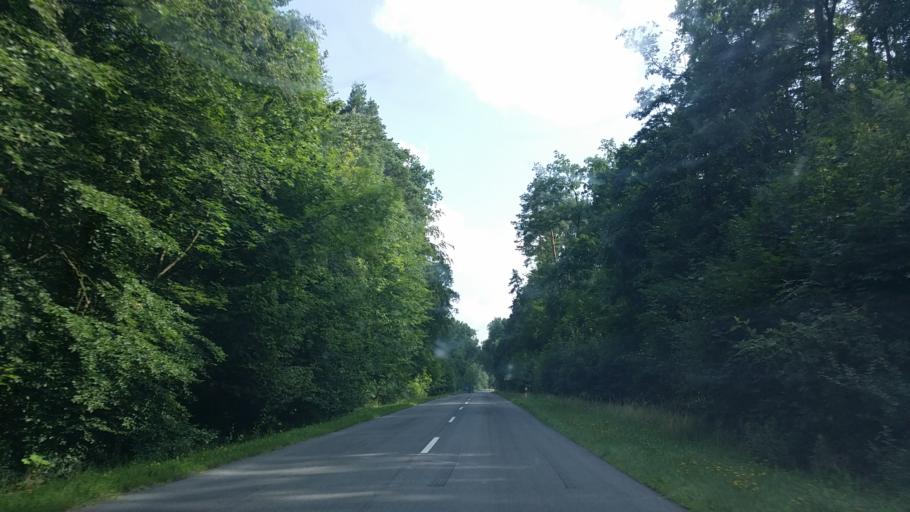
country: PL
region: Lubusz
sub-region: Powiat gorzowski
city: Klodawa
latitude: 52.8065
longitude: 15.2176
